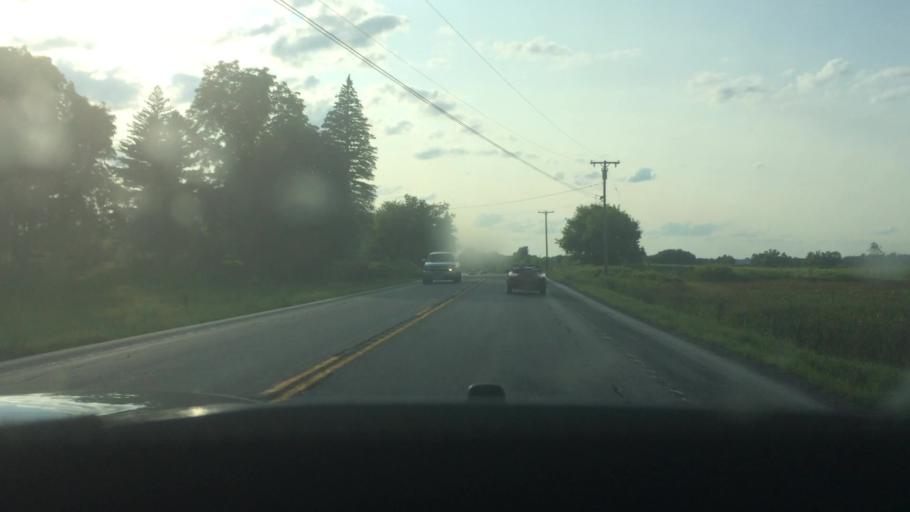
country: US
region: New York
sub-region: St. Lawrence County
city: Ogdensburg
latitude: 44.6589
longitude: -75.3284
